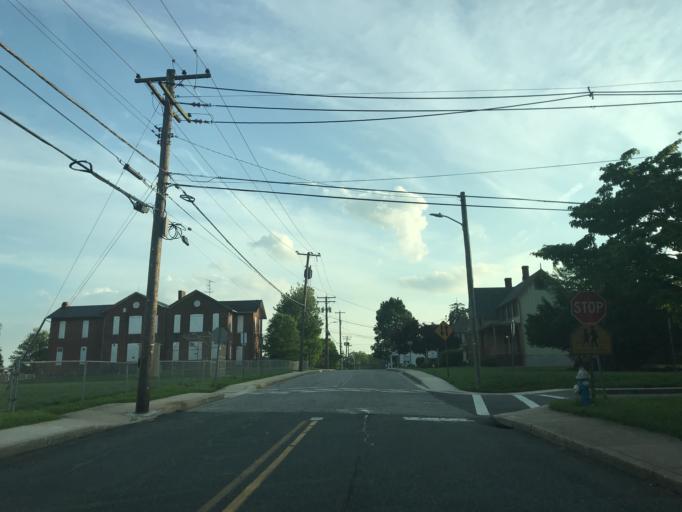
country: US
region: Maryland
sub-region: Harford County
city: North Bel Air
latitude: 39.5402
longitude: -76.3509
